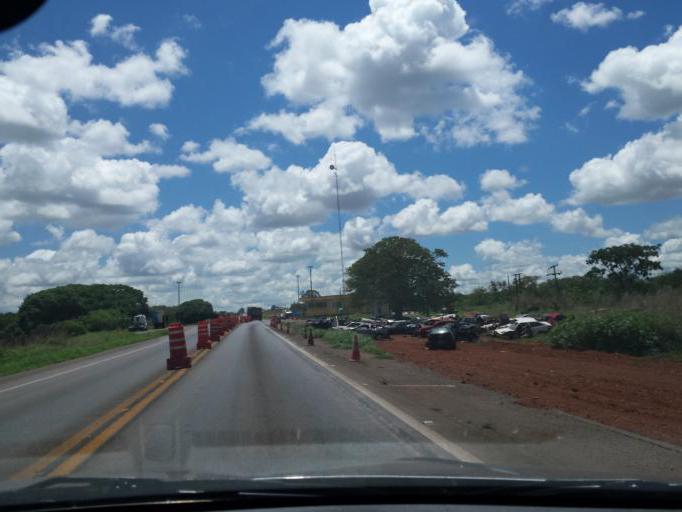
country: BR
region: Goias
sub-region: Cristalina
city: Cristalina
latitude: -16.7129
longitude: -47.6708
